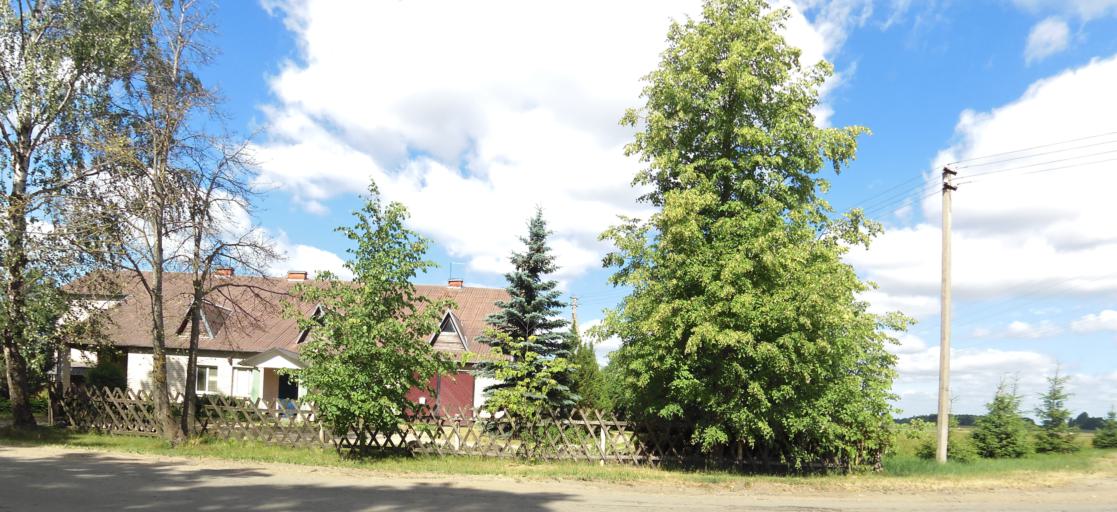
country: LT
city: Vabalninkas
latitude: 56.0227
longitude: 24.8051
